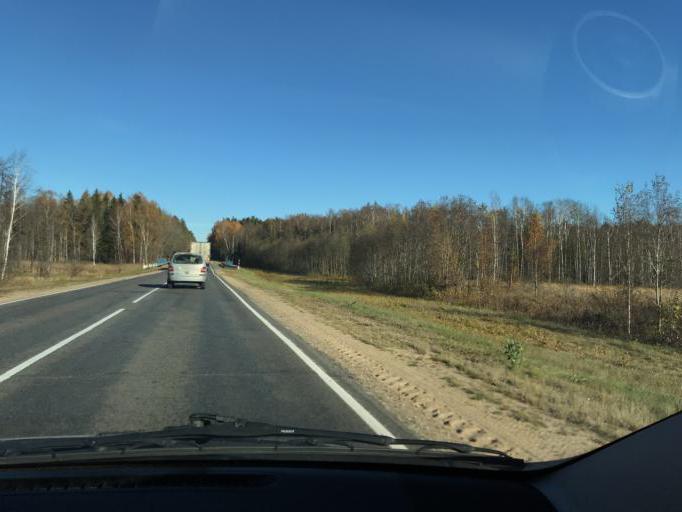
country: BY
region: Vitebsk
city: Polatsk
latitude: 55.3359
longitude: 28.7903
